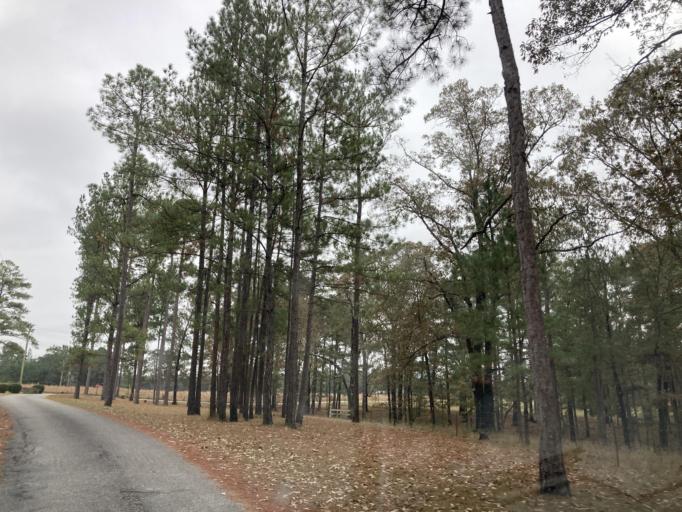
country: US
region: Mississippi
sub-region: Lamar County
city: Purvis
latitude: 31.1984
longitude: -89.4633
